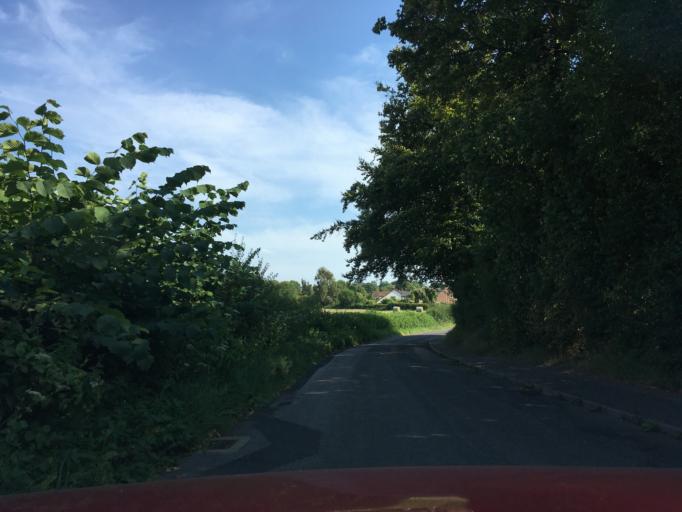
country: GB
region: England
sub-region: Gloucestershire
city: Dursley
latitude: 51.6943
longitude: -2.3535
